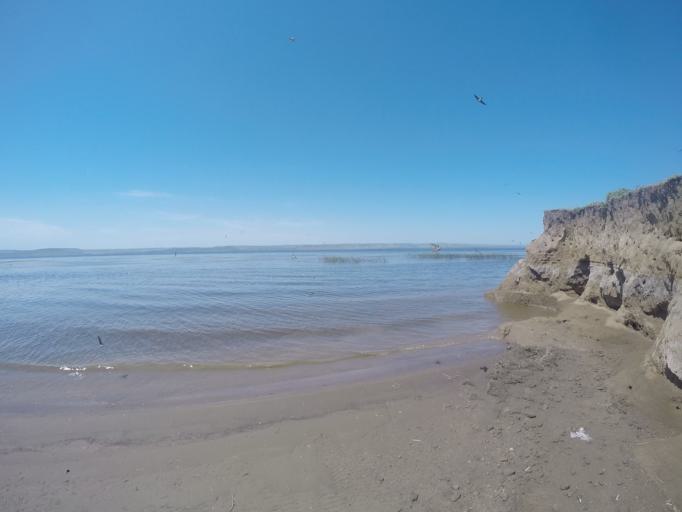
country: RU
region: Saratov
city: Krasnoarmeysk
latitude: 51.1673
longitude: 45.9033
